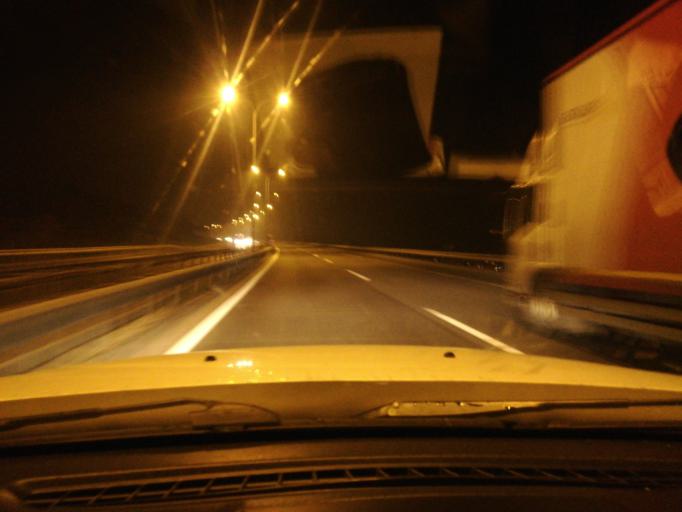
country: TR
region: Istanbul
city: Celaliye
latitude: 41.0507
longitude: 28.4404
